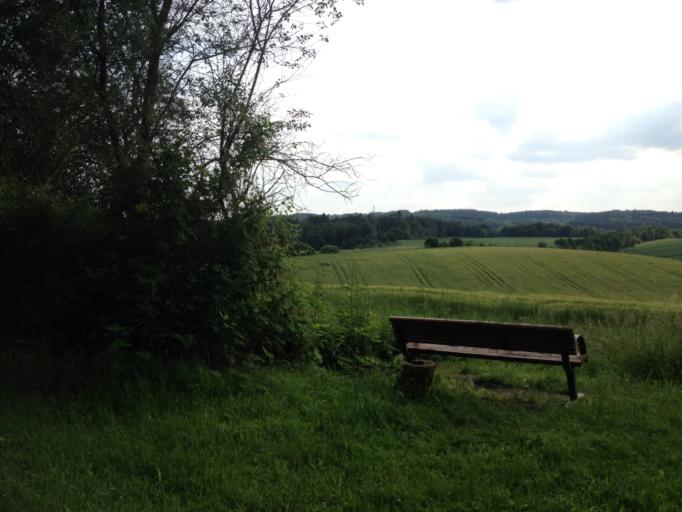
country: DE
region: Saarland
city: Namborn
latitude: 49.4703
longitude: 7.1193
